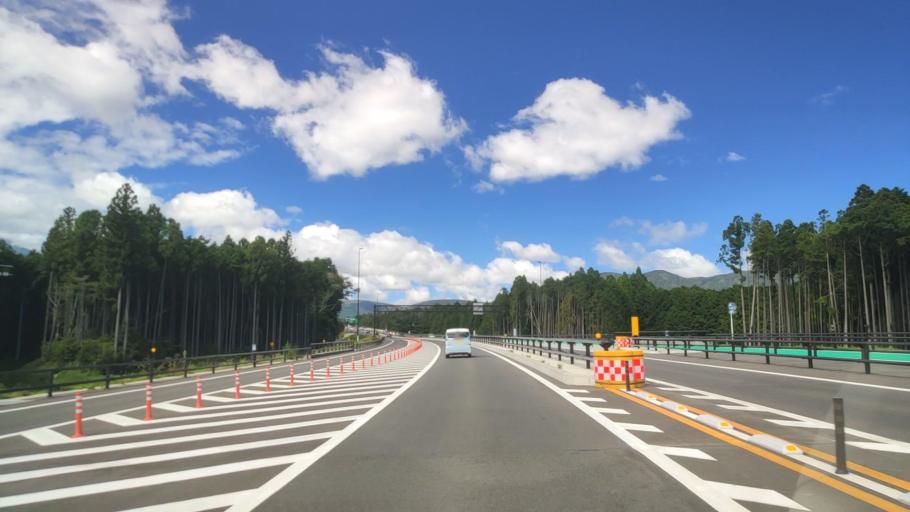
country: JP
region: Shizuoka
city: Gotemba
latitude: 35.3287
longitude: 138.9017
